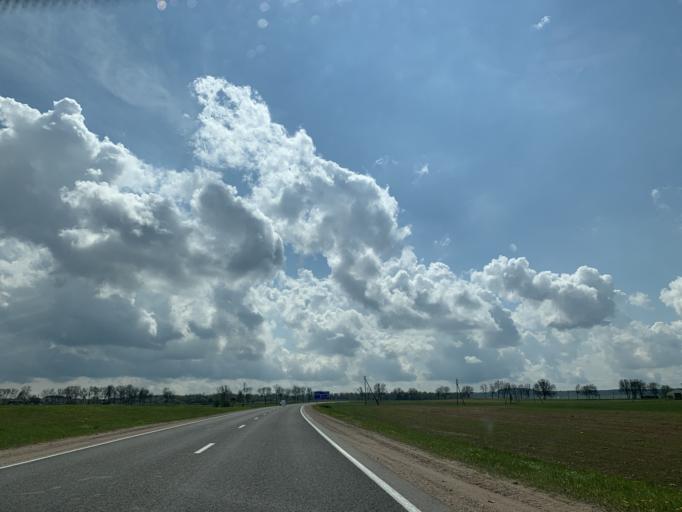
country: BY
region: Minsk
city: Nyasvizh
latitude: 53.2331
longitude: 26.7208
